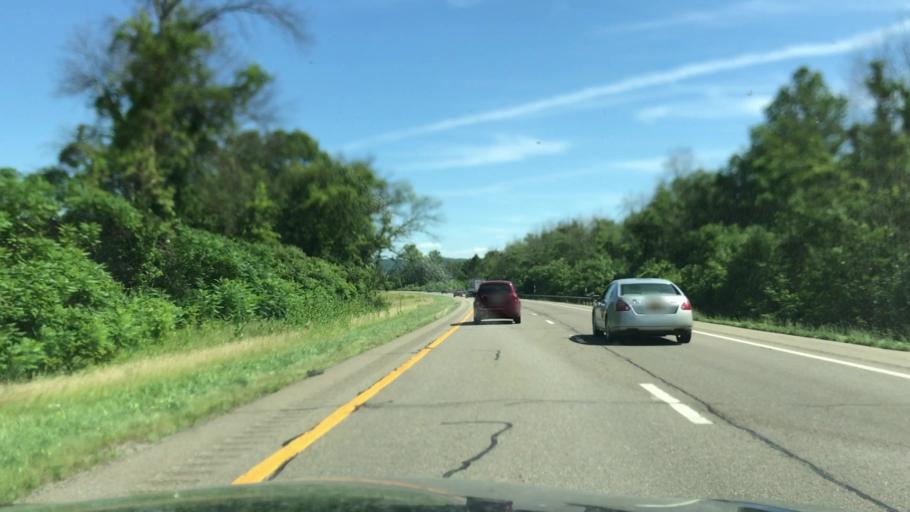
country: US
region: New York
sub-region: Steuben County
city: Gang Mills
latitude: 42.2173
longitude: -77.1777
